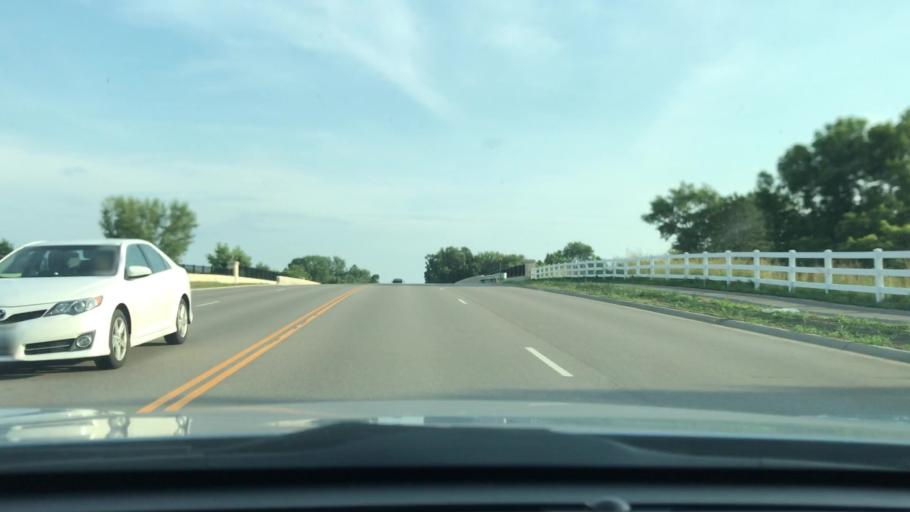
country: US
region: Minnesota
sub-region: Hennepin County
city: Maple Grove
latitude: 45.0509
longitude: -93.4818
